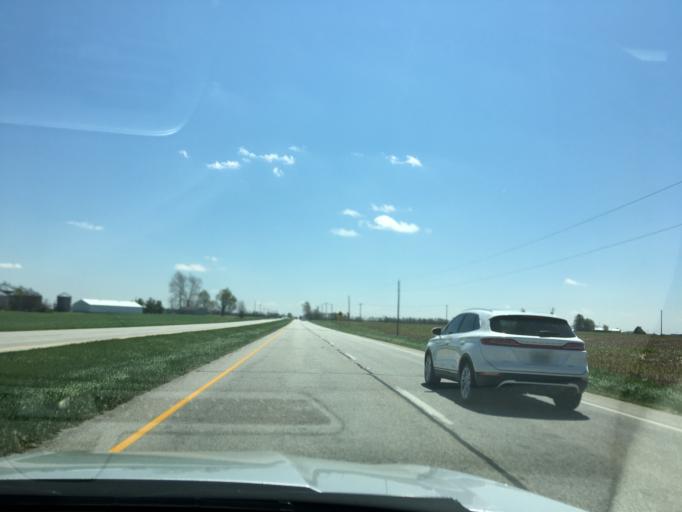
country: US
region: Indiana
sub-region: Clinton County
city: Mulberry
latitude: 40.2647
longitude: -86.7130
